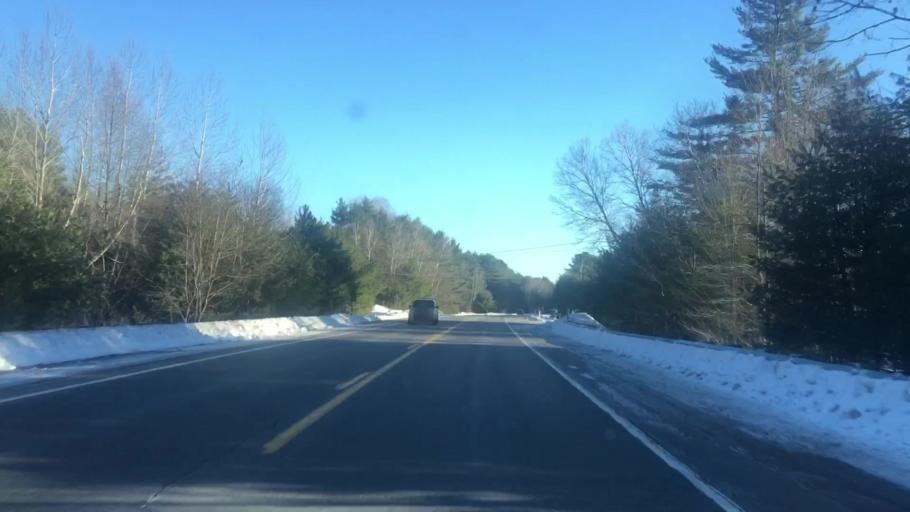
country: US
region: Maine
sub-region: Somerset County
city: Norridgewock
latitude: 44.6870
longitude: -69.7338
